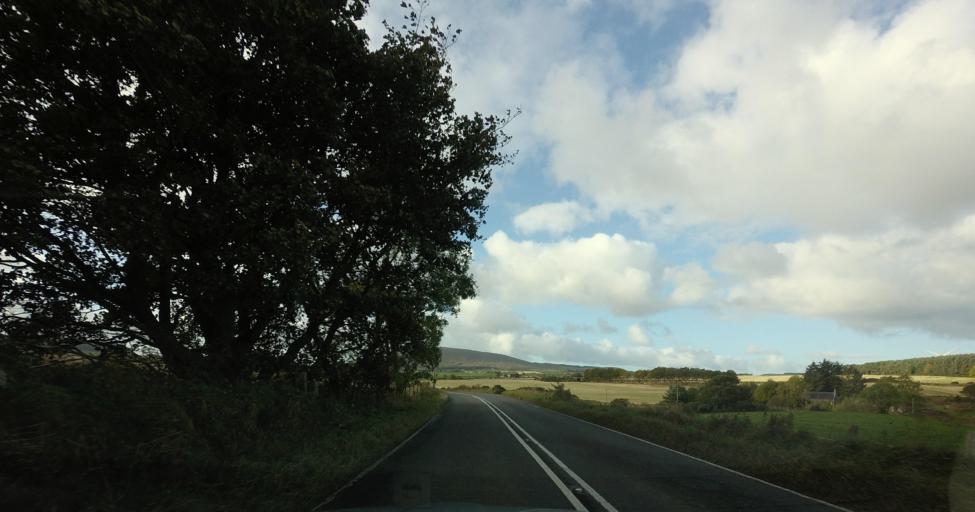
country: GB
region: Scotland
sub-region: Aberdeenshire
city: Portsoy
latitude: 57.6017
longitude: -2.7214
